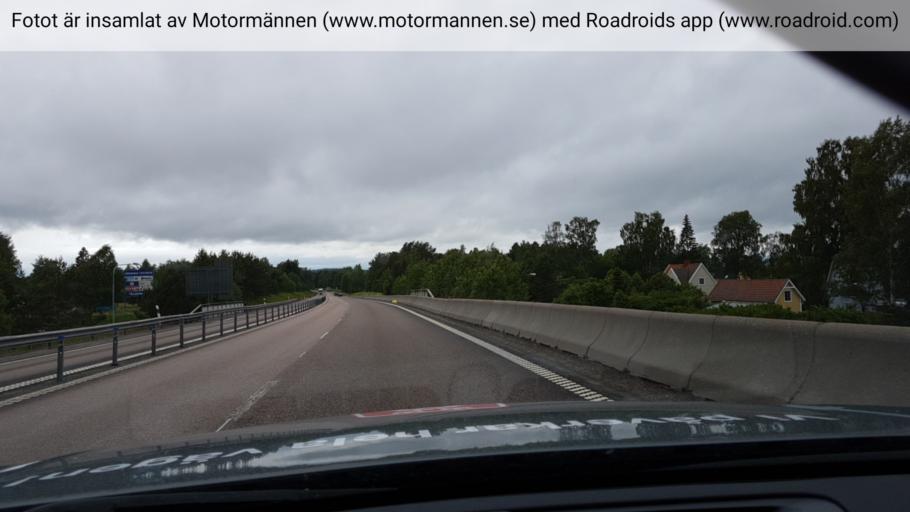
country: SE
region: Vaesternorrland
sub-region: Timra Kommun
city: Bergeforsen
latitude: 62.5162
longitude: 17.3804
